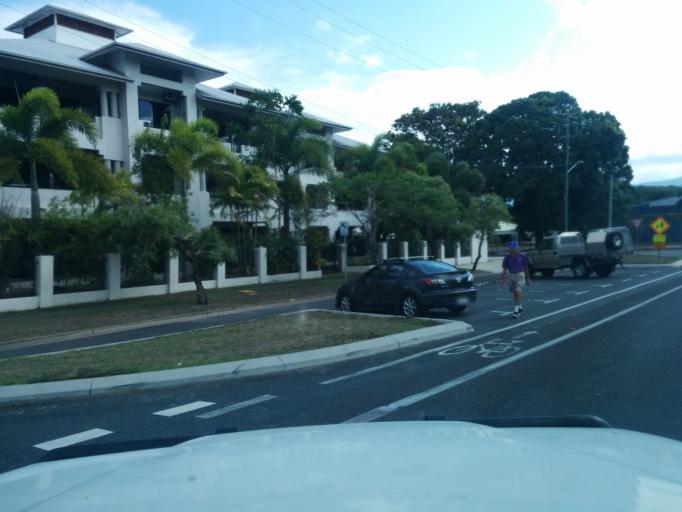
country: AU
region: Queensland
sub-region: Cairns
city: Cairns
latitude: -16.9232
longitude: 145.7636
